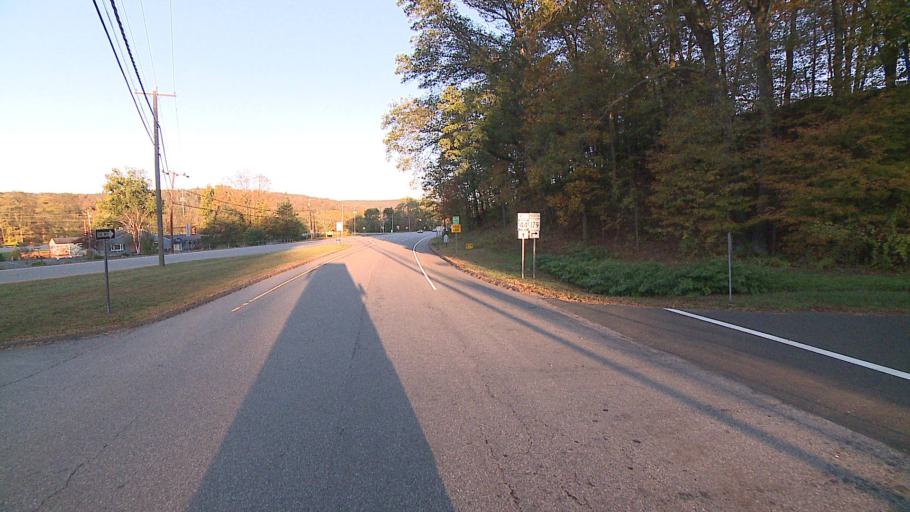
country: US
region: Connecticut
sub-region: Hartford County
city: Collinsville
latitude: 41.8341
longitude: -72.9258
